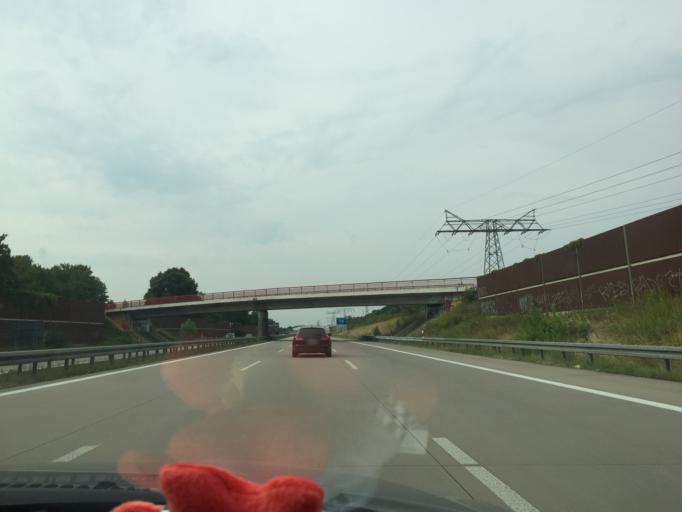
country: DE
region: Brandenburg
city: Neuenhagen
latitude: 52.5151
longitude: 13.7278
